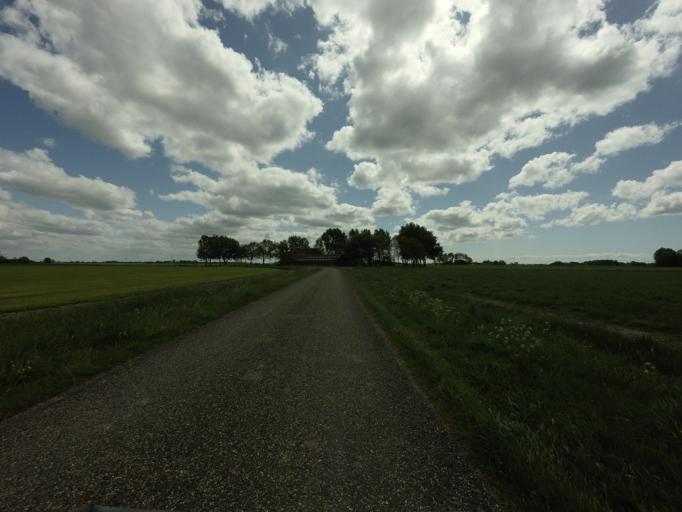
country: NL
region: Friesland
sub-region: Gemeente Franekeradeel
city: Tzum
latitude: 53.1379
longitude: 5.5578
